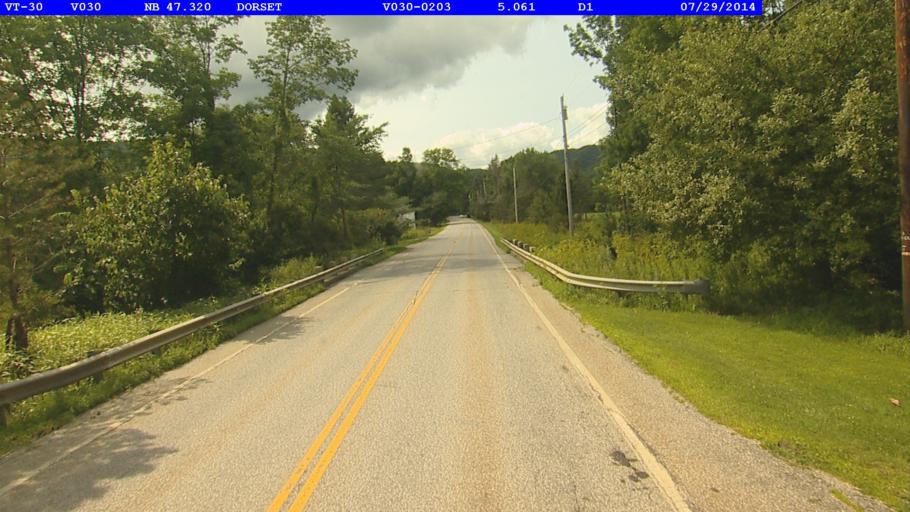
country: US
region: Vermont
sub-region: Bennington County
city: Manchester Center
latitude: 43.2705
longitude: -73.1199
